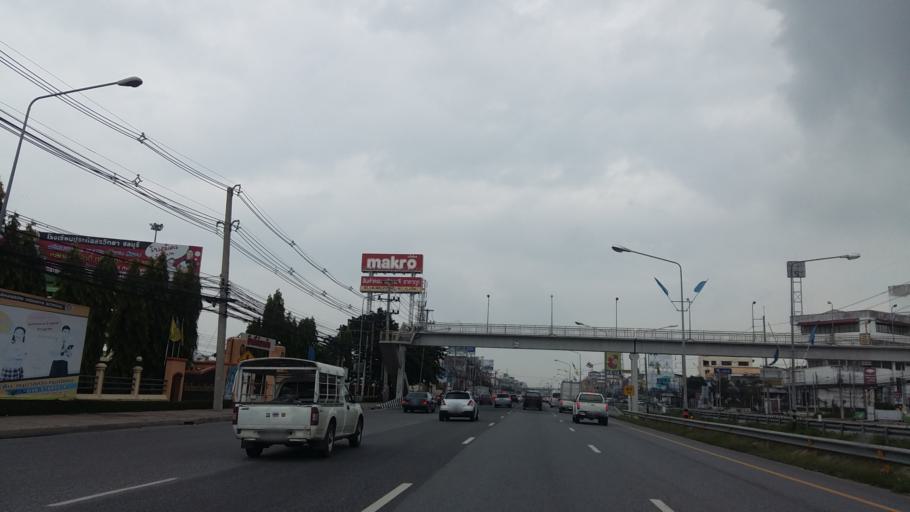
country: TH
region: Chon Buri
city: Chon Buri
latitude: 13.3201
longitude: 100.9609
